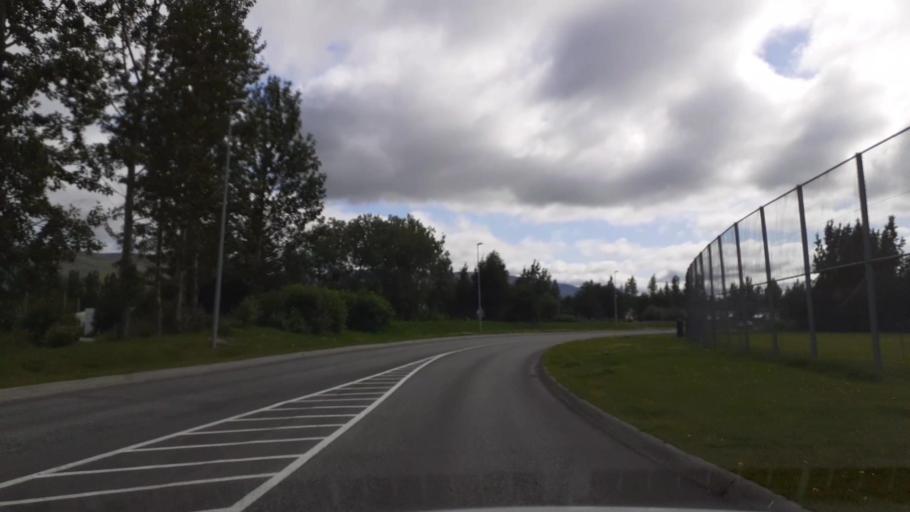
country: IS
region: Northeast
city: Akureyri
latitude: 65.6766
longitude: -18.1117
